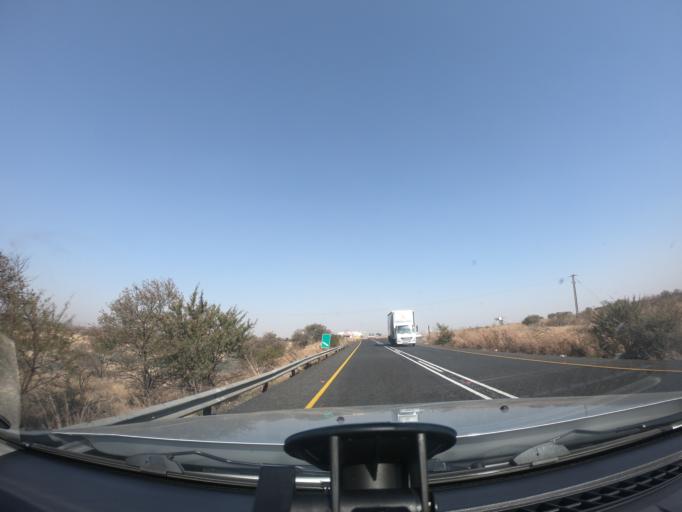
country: ZA
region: KwaZulu-Natal
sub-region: uThukela District Municipality
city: Ladysmith
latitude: -28.7268
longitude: 29.8099
